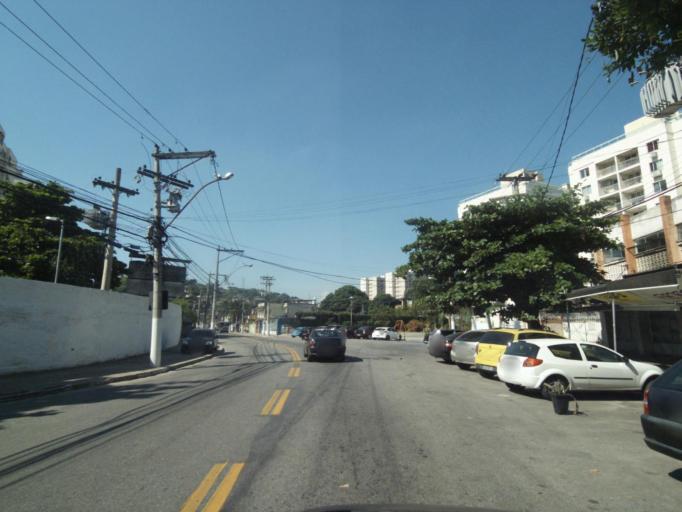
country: BR
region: Rio de Janeiro
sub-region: Niteroi
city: Niteroi
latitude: -22.8626
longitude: -43.0958
